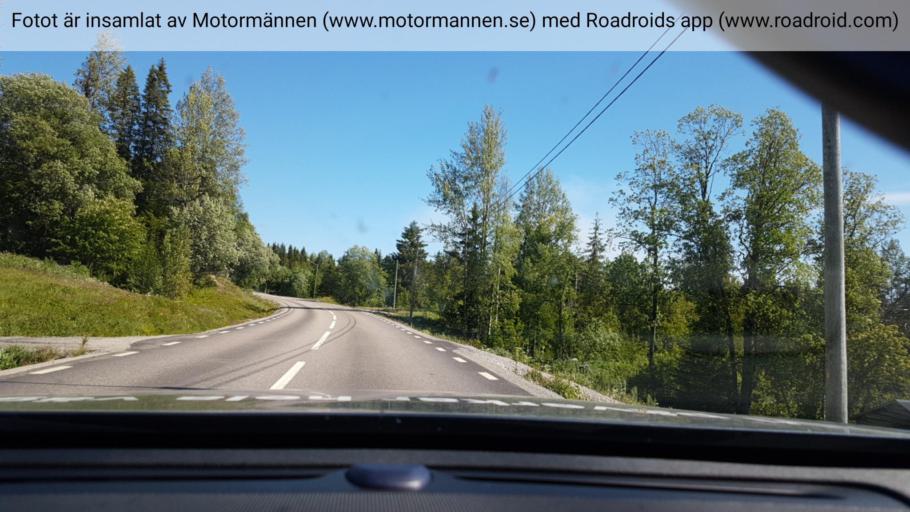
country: SE
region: Vaesterbotten
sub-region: Asele Kommun
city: Insjon
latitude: 64.7145
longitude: 17.6852
